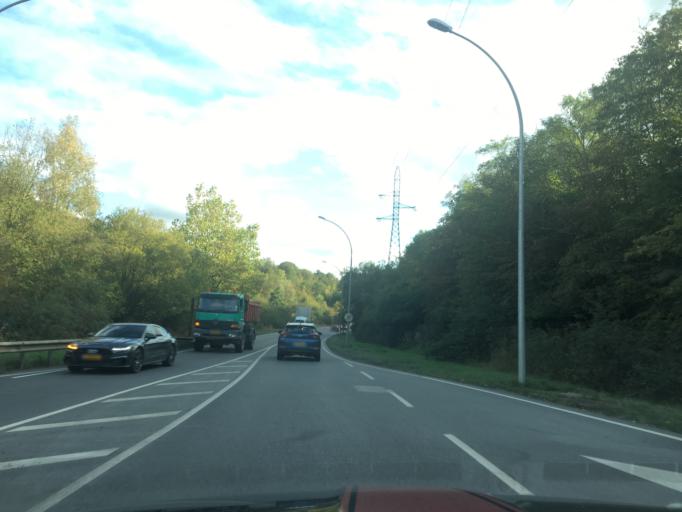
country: LU
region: Luxembourg
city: Soleuvre
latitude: 49.5323
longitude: 5.9277
